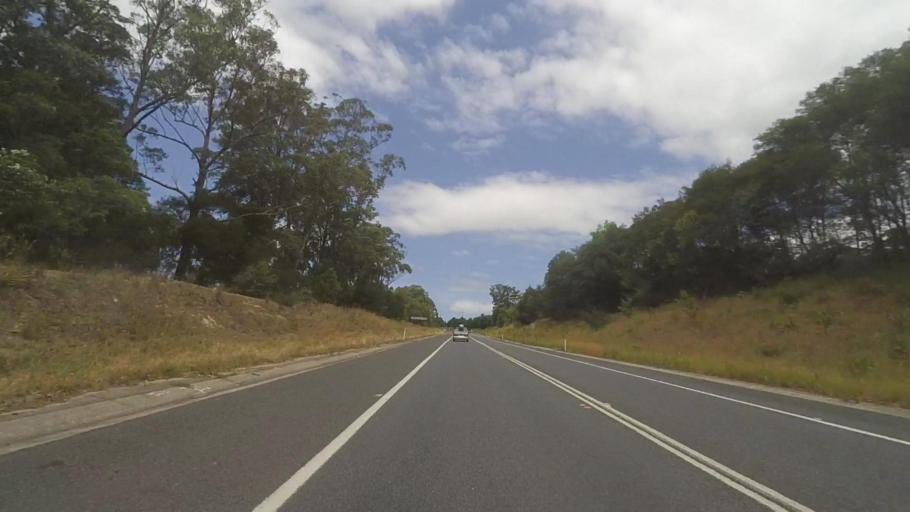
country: AU
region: New South Wales
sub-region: Shoalhaven Shire
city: Milton
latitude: -35.2168
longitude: 150.4348
